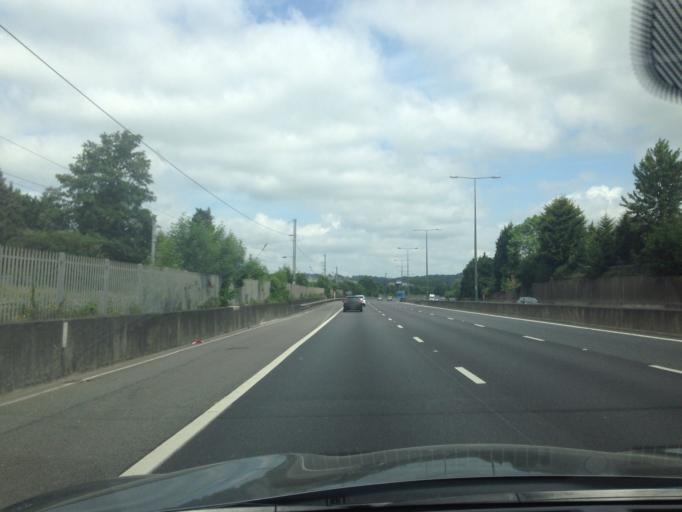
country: GB
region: England
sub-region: Greater London
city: Edgware
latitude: 51.6235
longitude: -0.2590
